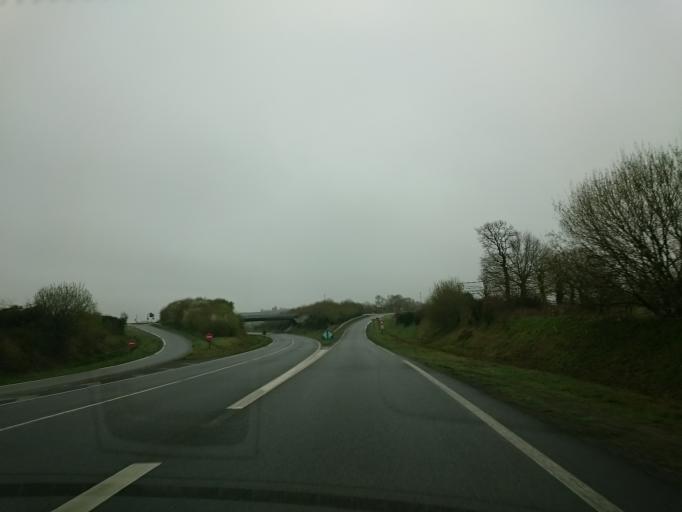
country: FR
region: Brittany
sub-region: Departement d'Ille-et-Vilaine
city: Bourg-des-Comptes
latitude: 47.9312
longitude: -1.7303
